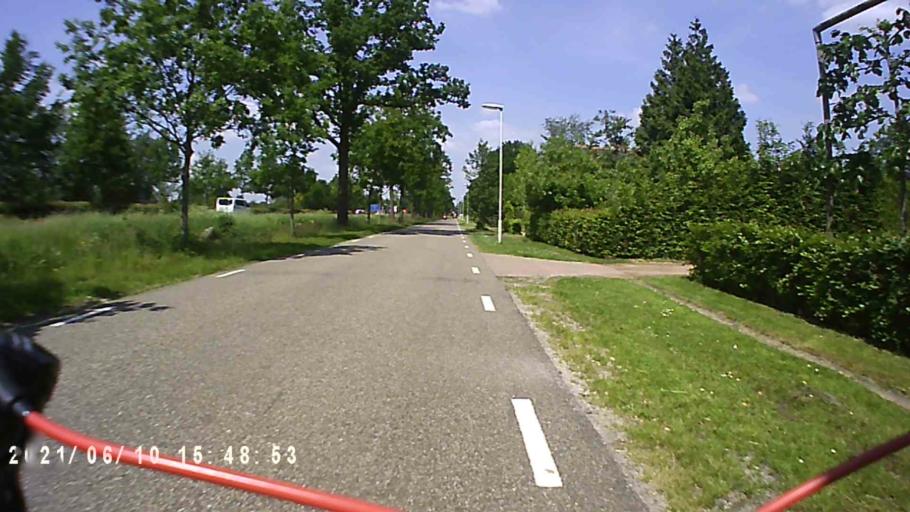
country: NL
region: Friesland
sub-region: Gemeente Achtkarspelen
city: Harkema
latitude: 53.1663
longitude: 6.1190
